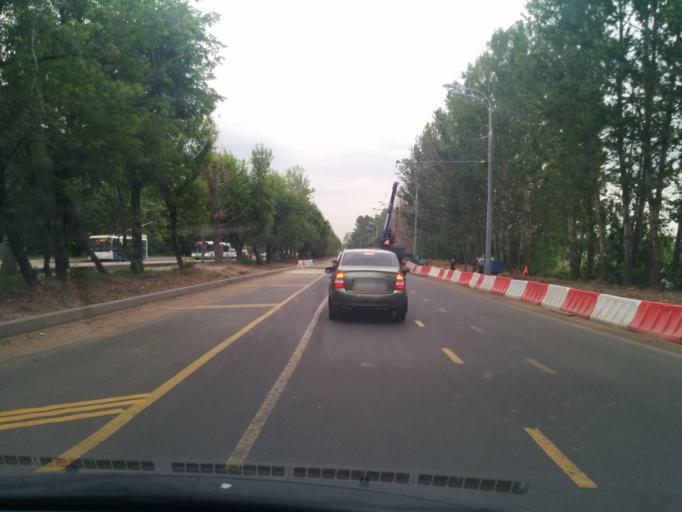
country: RU
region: Moscow
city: Likhobory
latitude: 55.8408
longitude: 37.5503
